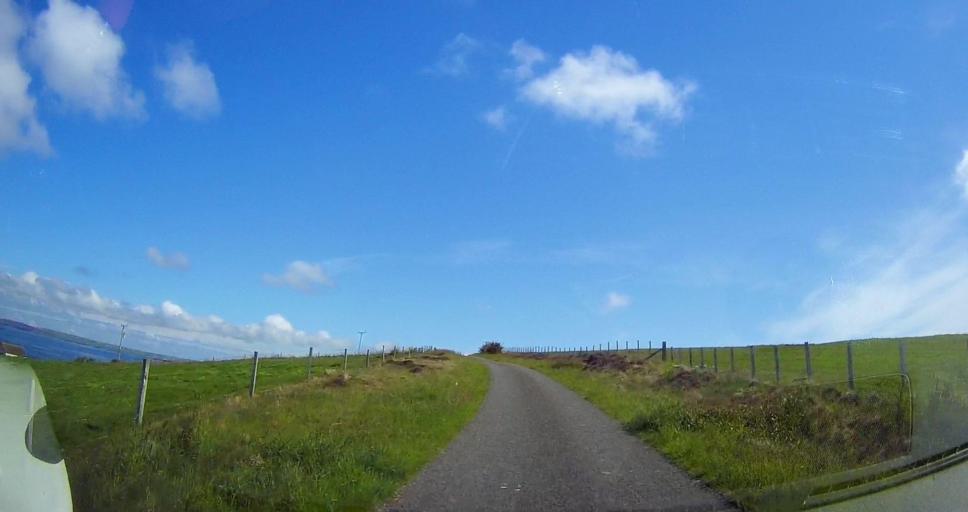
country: GB
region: Scotland
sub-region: Orkney Islands
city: Orkney
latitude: 58.8535
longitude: -2.9524
